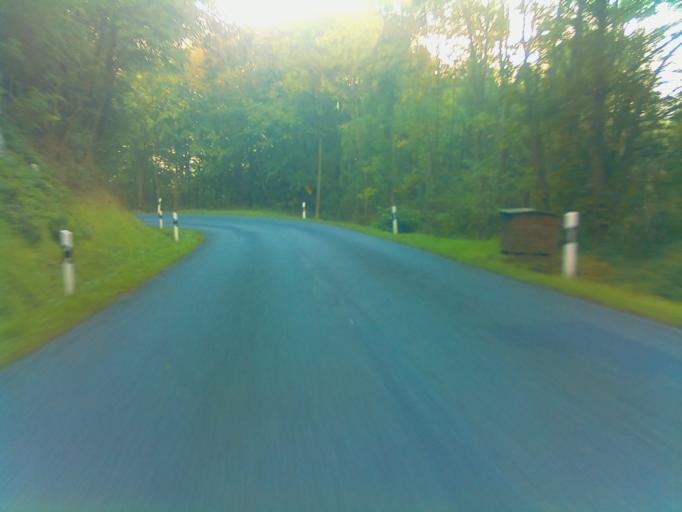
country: DE
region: Thuringia
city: Kahla
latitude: 50.8027
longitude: 11.5980
